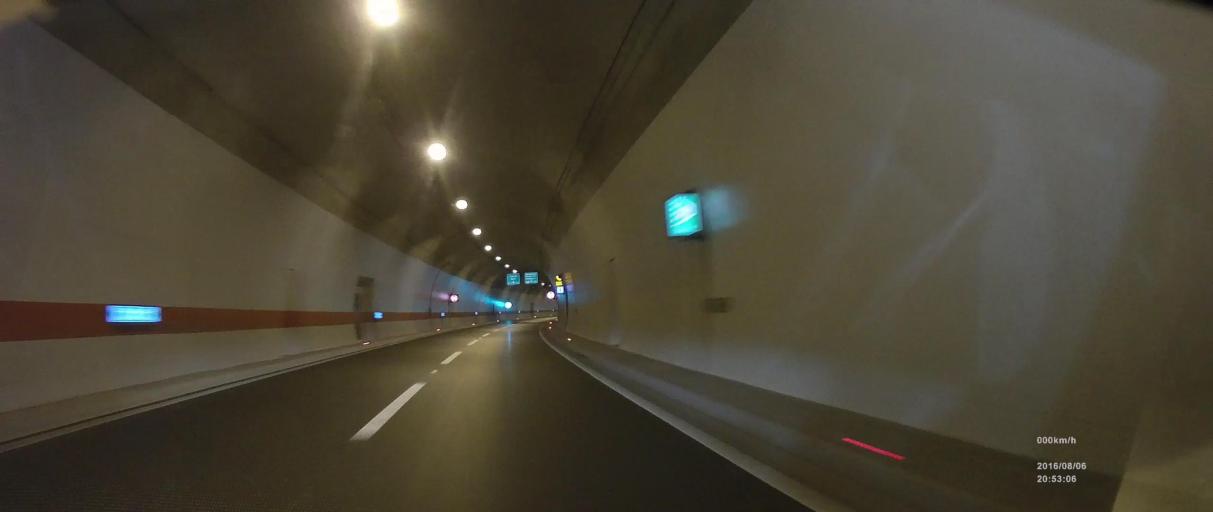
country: BA
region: Federation of Bosnia and Herzegovina
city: Ljubuski
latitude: 43.1386
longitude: 17.4837
